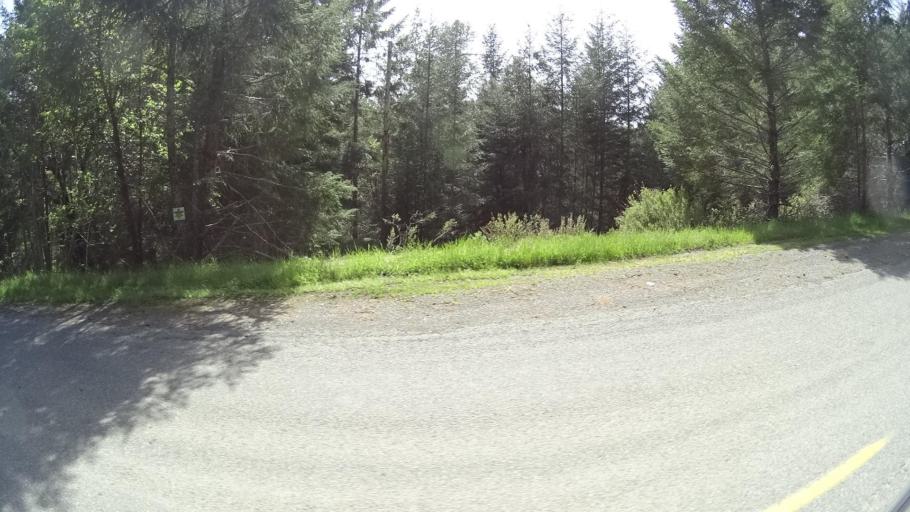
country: US
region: California
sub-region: Humboldt County
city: Redway
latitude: 40.3978
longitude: -123.7464
